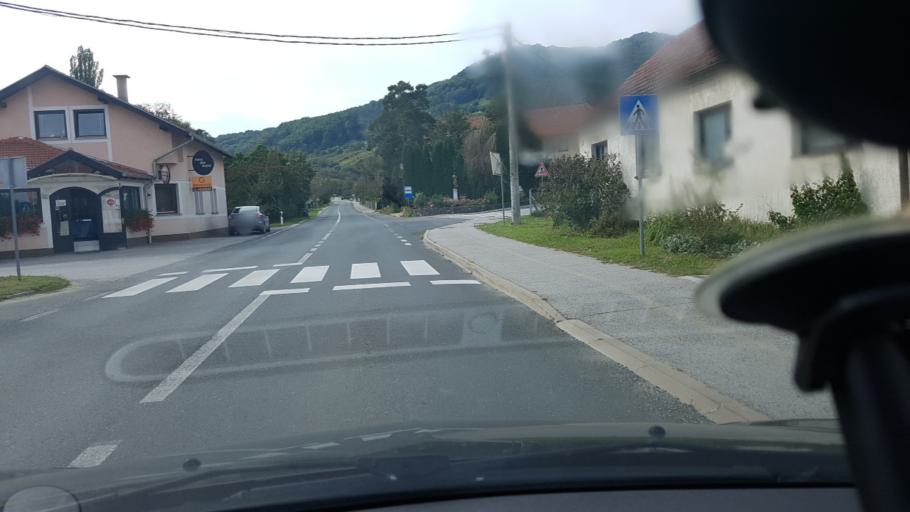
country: HR
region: Varazdinska
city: Remetinec
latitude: 46.1674
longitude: 16.3101
